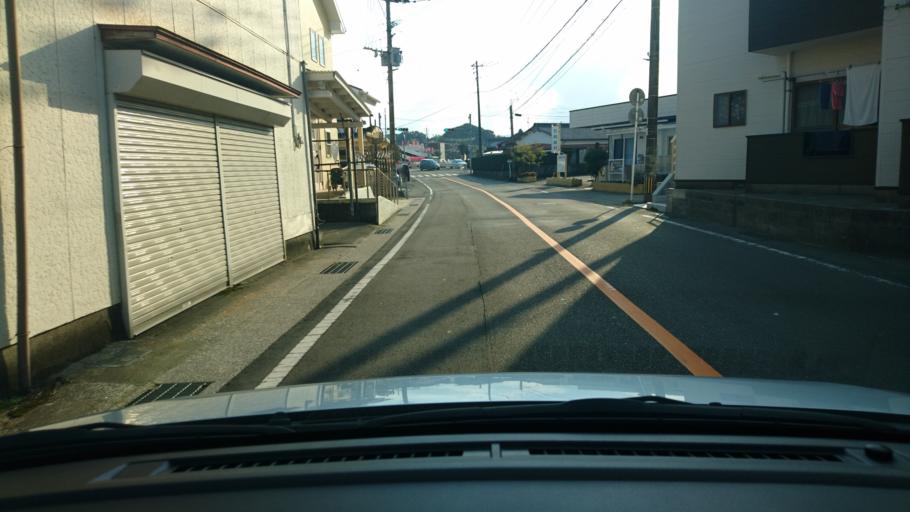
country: JP
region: Miyazaki
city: Miyazaki-shi
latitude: 31.8898
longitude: 131.4144
